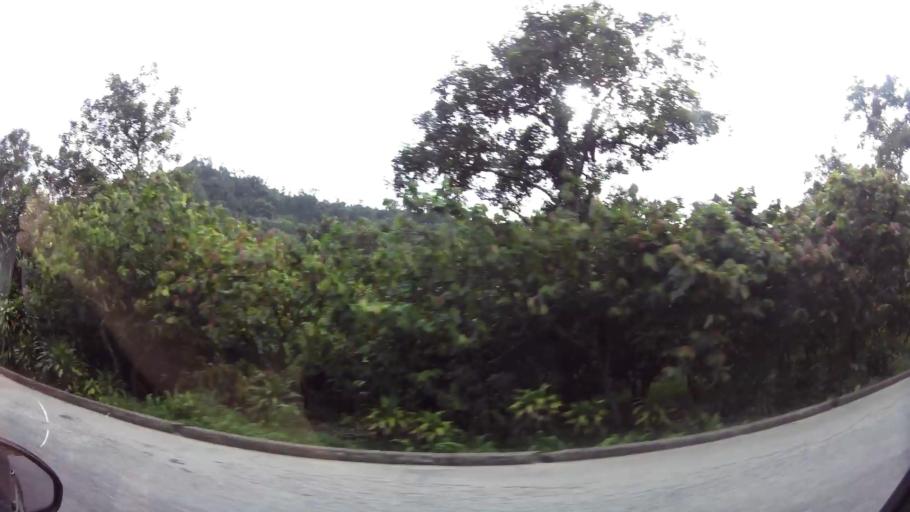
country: TT
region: San Juan/Laventille
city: Laventille
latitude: 10.6847
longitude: -61.4587
